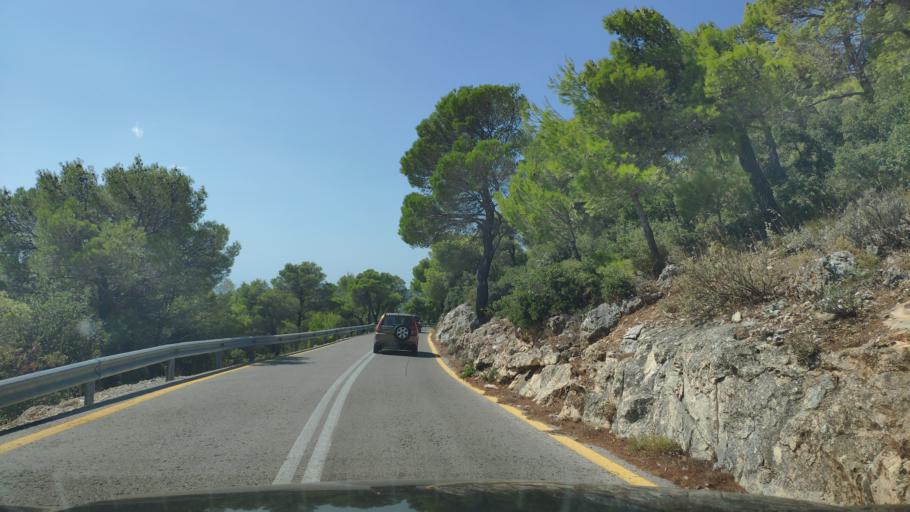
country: GR
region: Attica
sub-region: Nomarchia Anatolikis Attikis
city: Thrakomakedones
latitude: 38.1413
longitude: 23.7312
